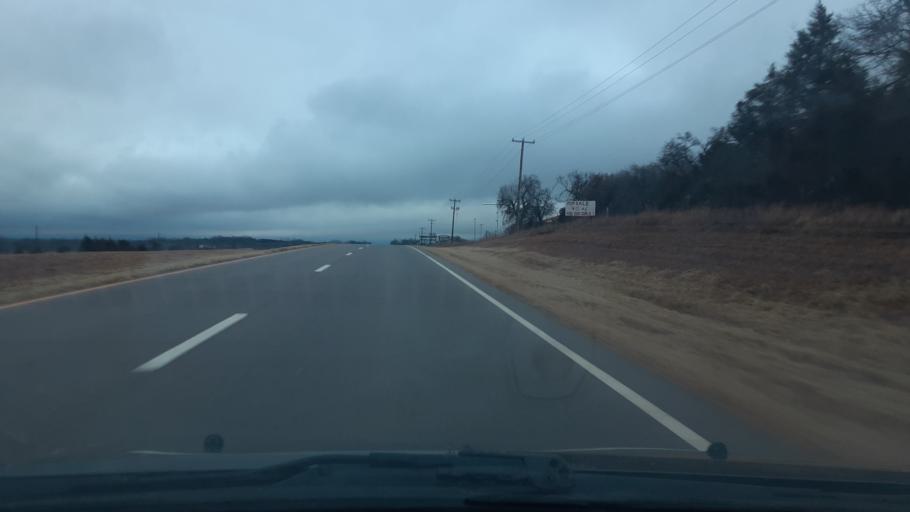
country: US
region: Oklahoma
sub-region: Payne County
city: Stillwater
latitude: 36.1158
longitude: -97.1655
